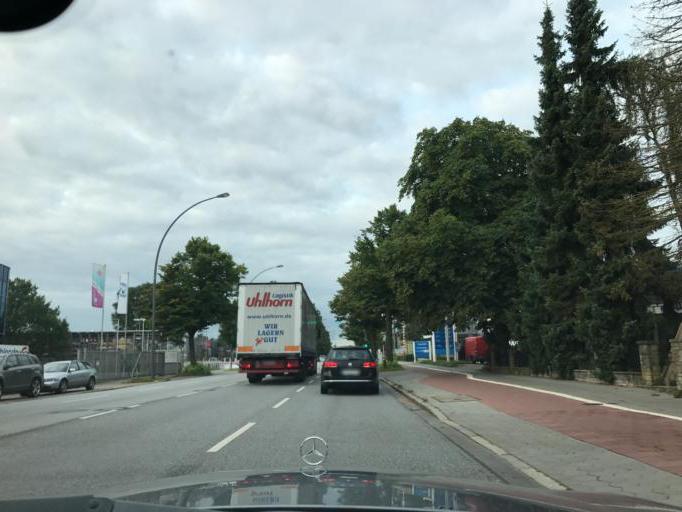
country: DE
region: Hamburg
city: Bergedorf
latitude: 53.4822
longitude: 10.2086
